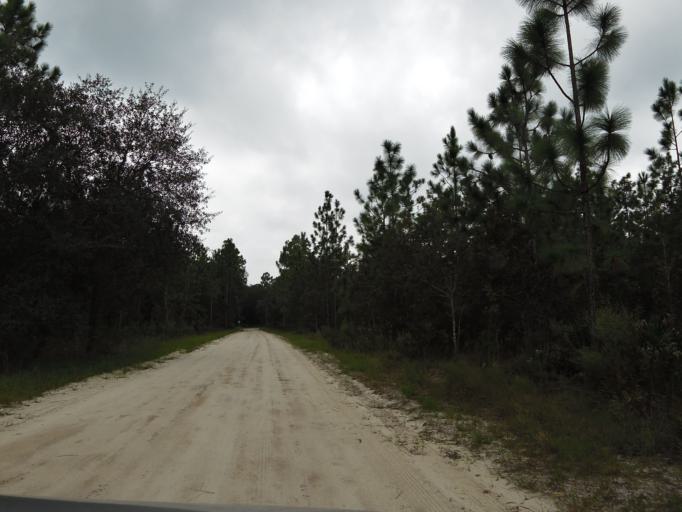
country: US
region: Florida
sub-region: Clay County
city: Middleburg
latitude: 30.1307
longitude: -81.9493
